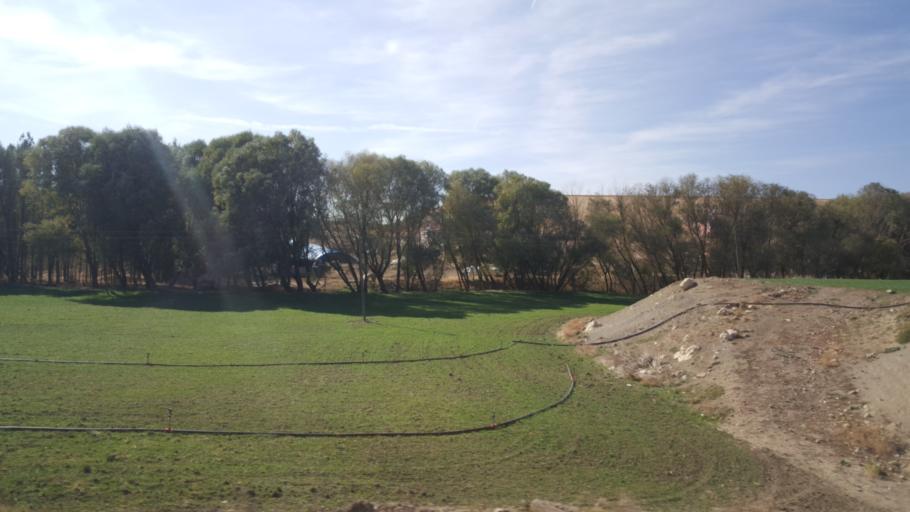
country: TR
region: Ankara
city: Haymana
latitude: 39.4177
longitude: 32.5958
